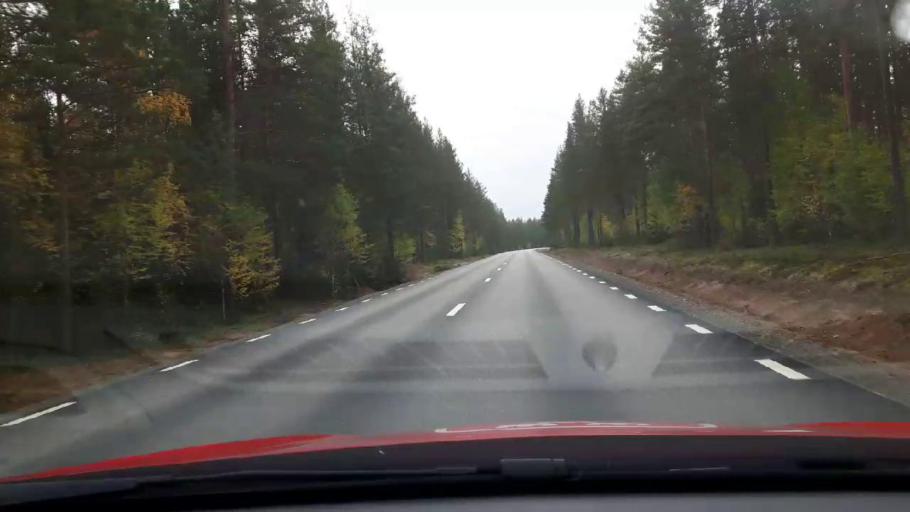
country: SE
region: Gaevleborg
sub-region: Ljusdals Kommun
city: Farila
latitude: 61.8541
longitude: 15.7482
